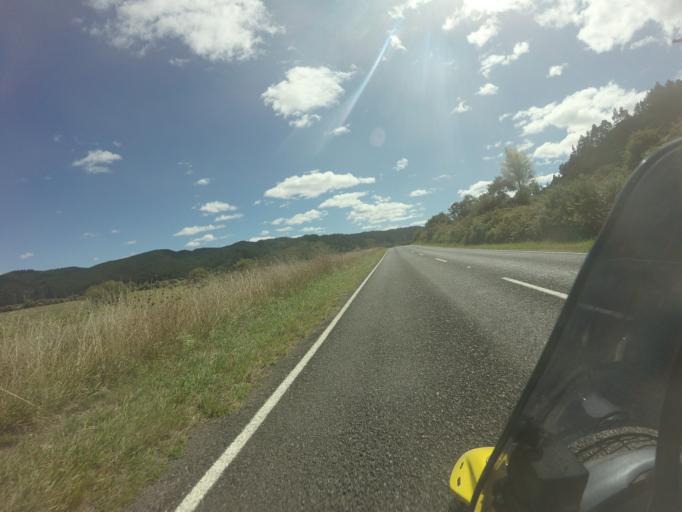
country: NZ
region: Bay of Plenty
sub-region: Kawerau District
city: Kawerau
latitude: -38.1891
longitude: 176.8394
